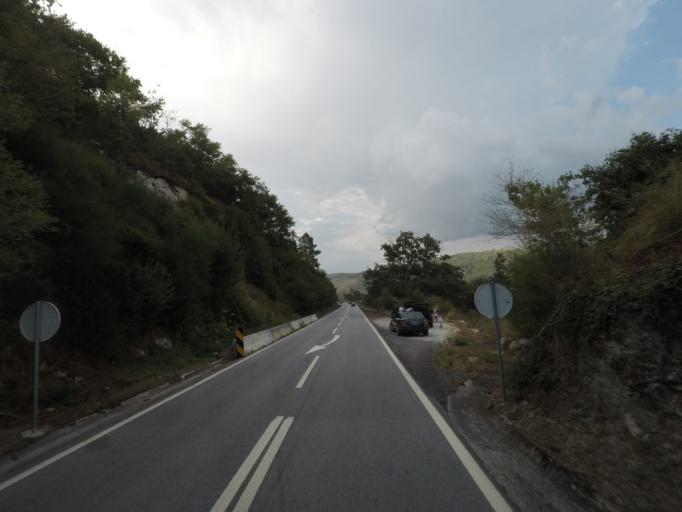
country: PT
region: Porto
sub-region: Baiao
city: Valadares
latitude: 41.2026
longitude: -7.9700
